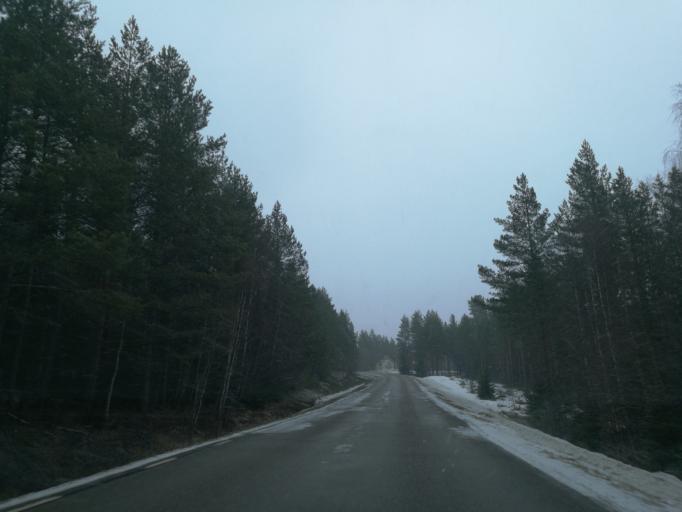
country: NO
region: Hedmark
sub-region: Grue
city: Kirkenaer
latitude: 60.6991
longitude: 12.5800
